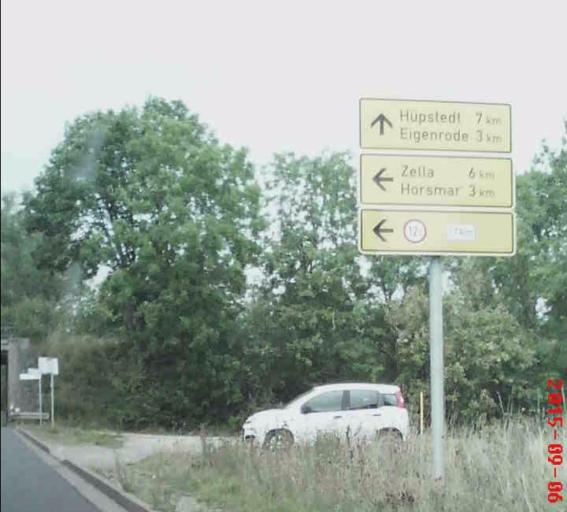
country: DE
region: Thuringia
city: Muehlhausen
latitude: 51.2660
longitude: 10.4465
